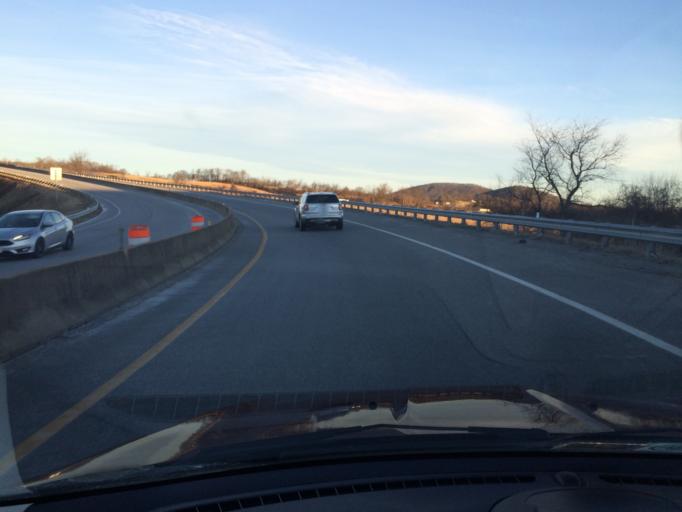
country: US
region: Virginia
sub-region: Augusta County
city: Jolivue
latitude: 38.1058
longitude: -79.0597
